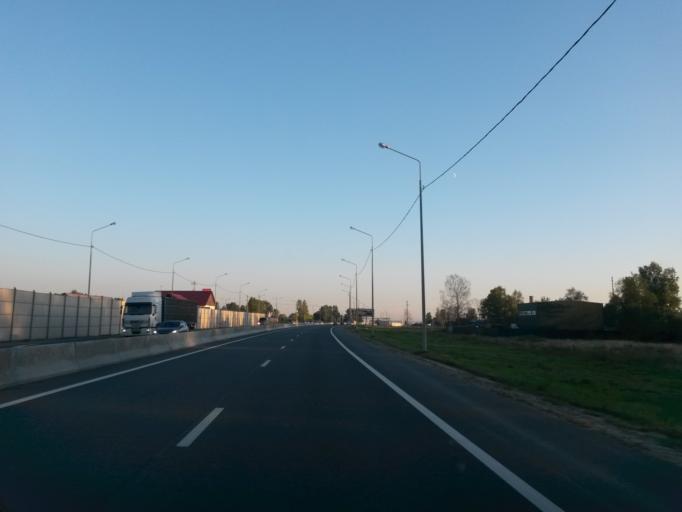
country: RU
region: Jaroslavl
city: Yaroslavl
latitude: 57.7127
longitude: 39.9032
